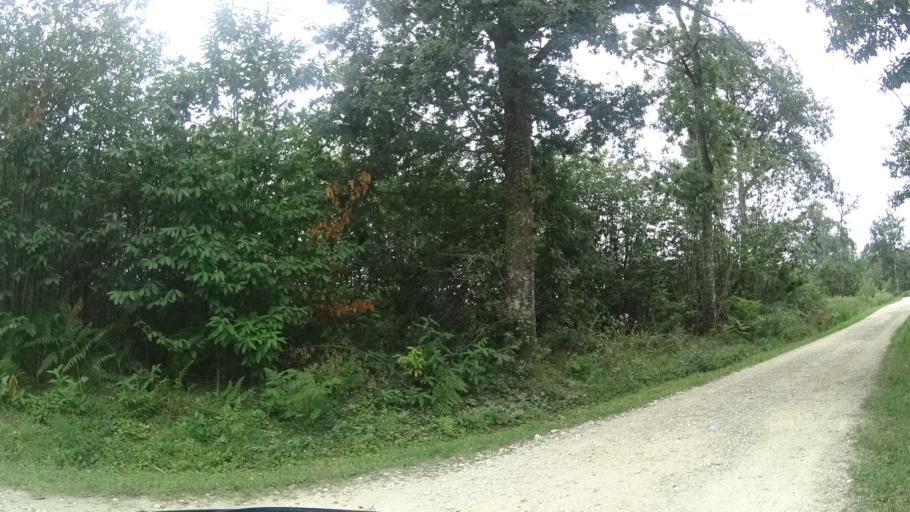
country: FR
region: Aquitaine
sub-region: Departement de la Dordogne
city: Neuvic
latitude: 45.0088
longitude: 0.5529
